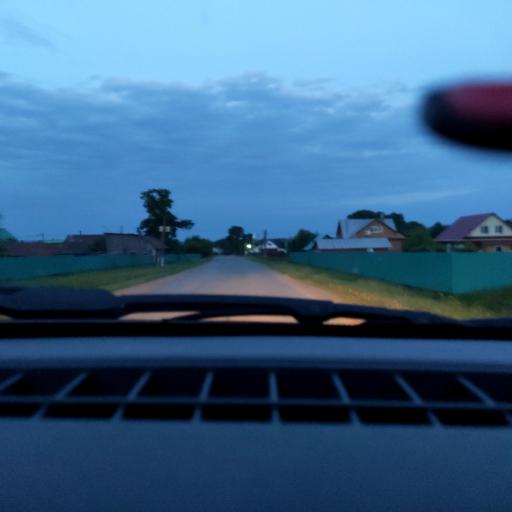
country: RU
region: Bashkortostan
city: Tolbazy
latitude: 54.2946
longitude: 55.8077
